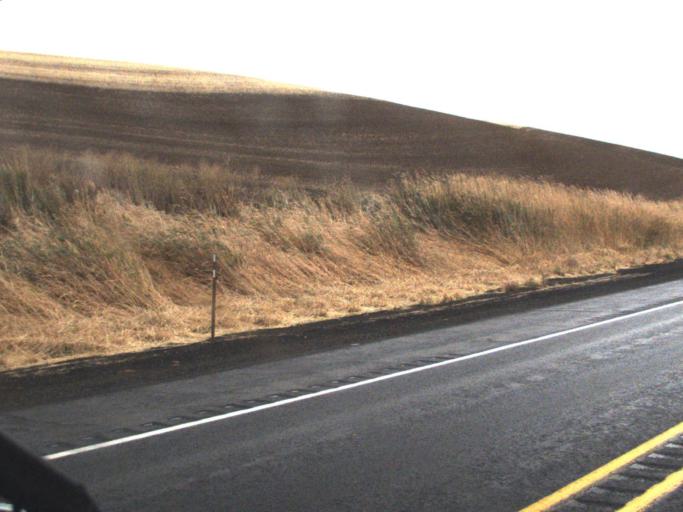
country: US
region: Washington
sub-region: Whitman County
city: Colfax
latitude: 46.7965
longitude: -117.3143
